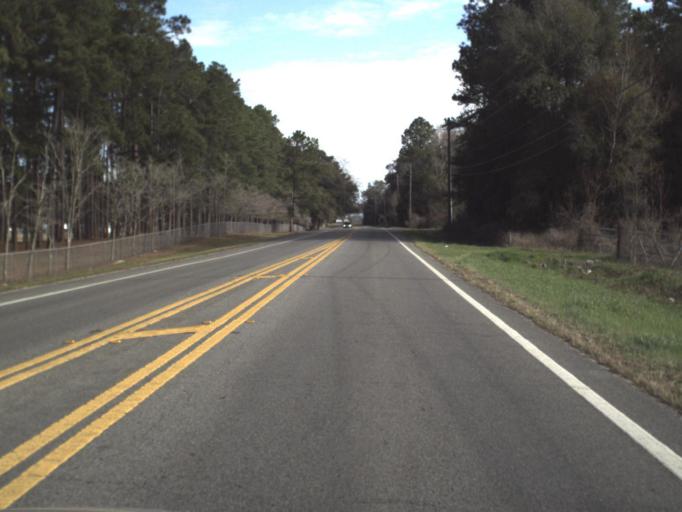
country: US
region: Florida
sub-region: Jackson County
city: Marianna
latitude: 30.8243
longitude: -85.1696
